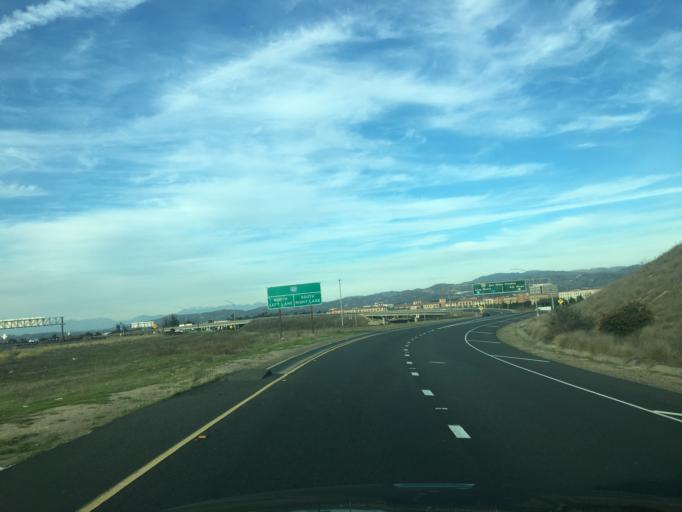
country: US
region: California
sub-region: Orange County
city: Laguna Woods
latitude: 33.6487
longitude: -117.7614
